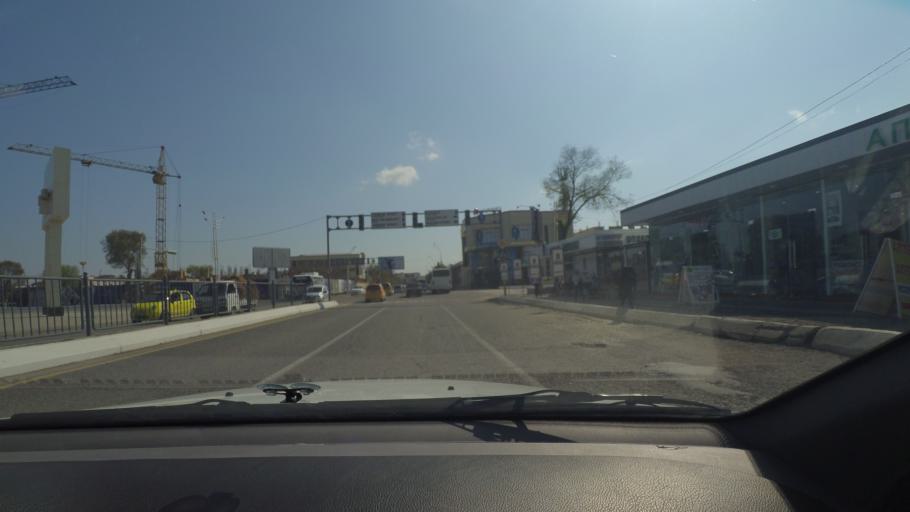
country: UZ
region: Bukhara
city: Bukhara
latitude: 39.7668
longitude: 64.4306
